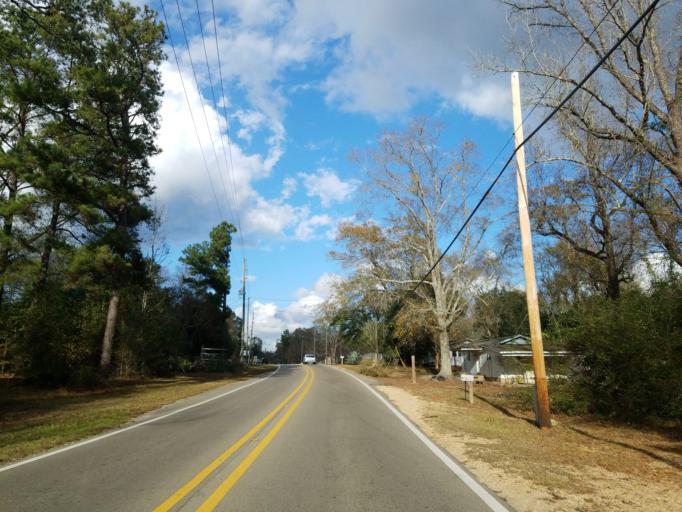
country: US
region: Mississippi
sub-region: Forrest County
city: Glendale
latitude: 31.3571
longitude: -89.3019
